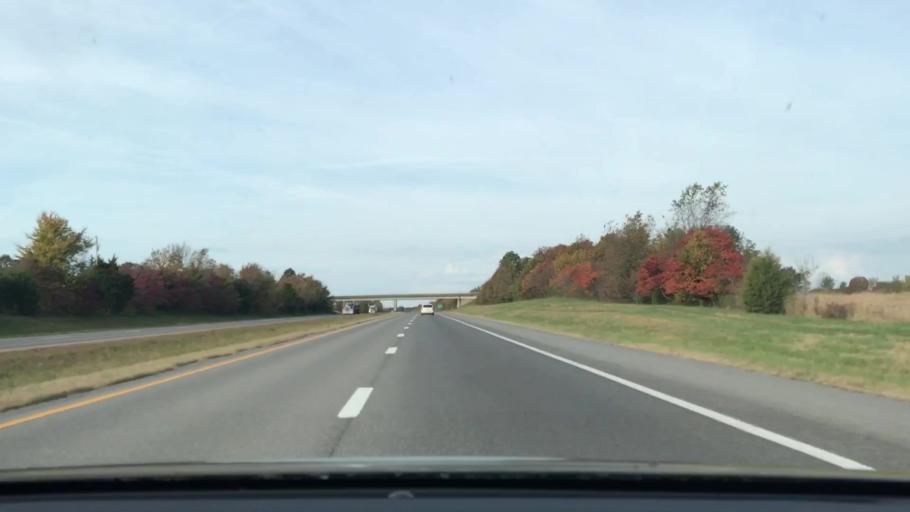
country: US
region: Kentucky
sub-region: Graves County
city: Mayfield
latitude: 36.7784
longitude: -88.5787
